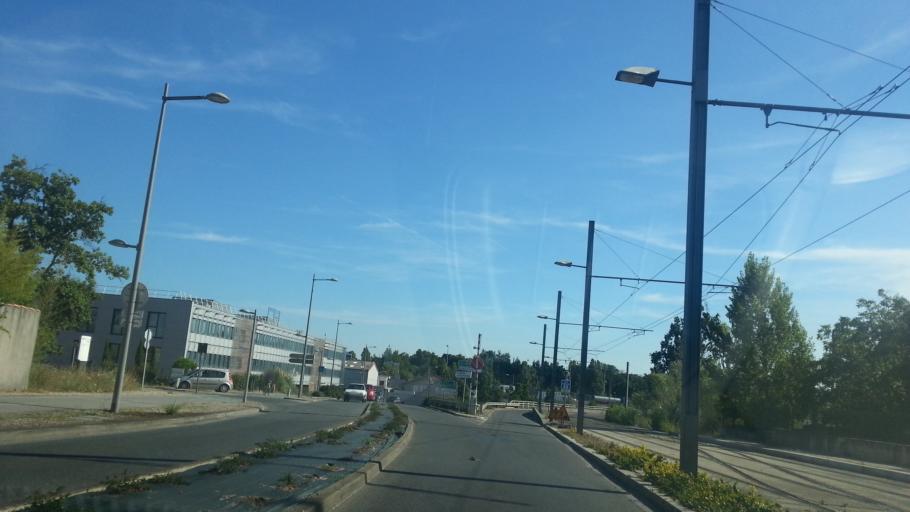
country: FR
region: Aquitaine
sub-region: Departement de la Gironde
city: Lormont
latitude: 44.8869
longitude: -0.5173
